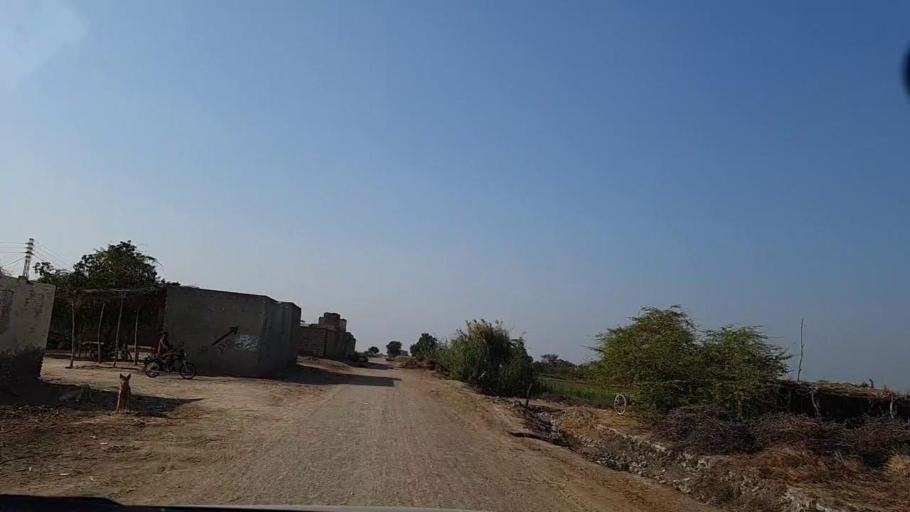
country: PK
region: Sindh
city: Mirwah Gorchani
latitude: 25.2225
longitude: 68.9906
